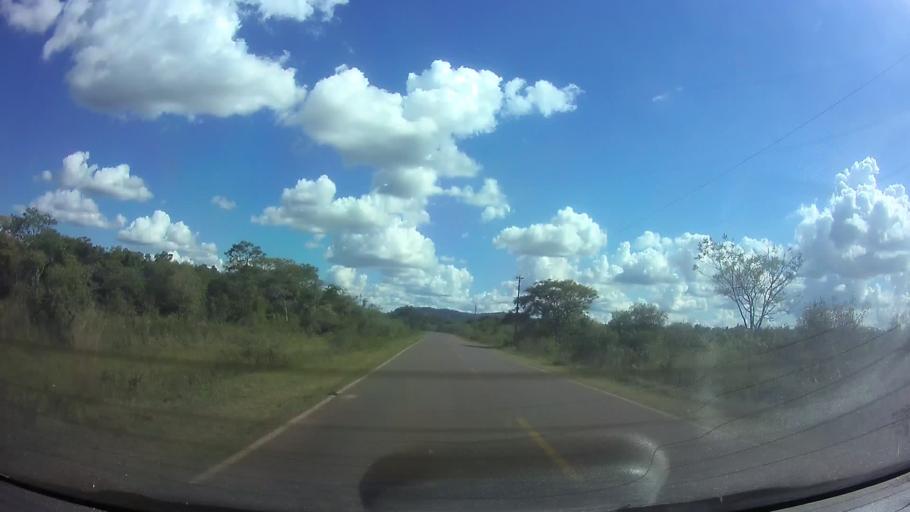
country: PY
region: Paraguari
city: Sapucai
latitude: -25.6818
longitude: -56.8631
